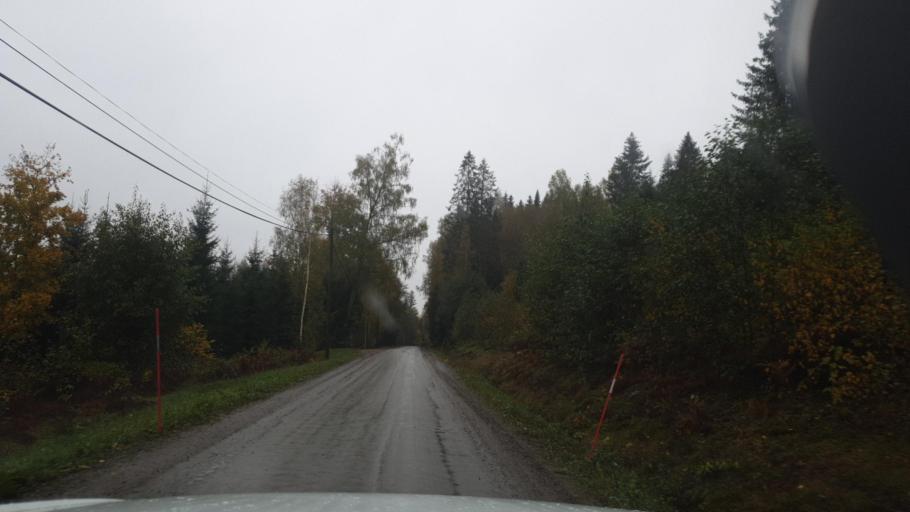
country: SE
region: Vaermland
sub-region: Eda Kommun
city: Amotfors
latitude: 59.7422
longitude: 12.2769
